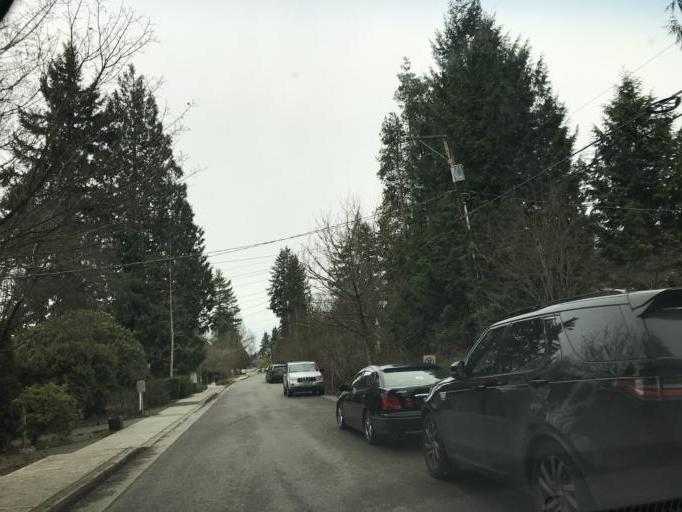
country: US
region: Washington
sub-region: King County
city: Lake Forest Park
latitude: 47.7114
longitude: -122.3043
